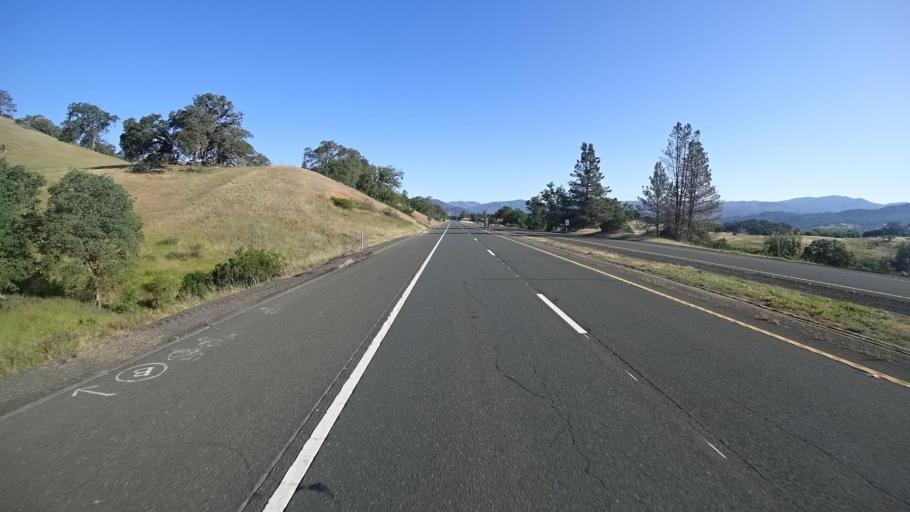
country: US
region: California
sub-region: Lake County
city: North Lakeport
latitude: 39.1264
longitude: -122.9072
